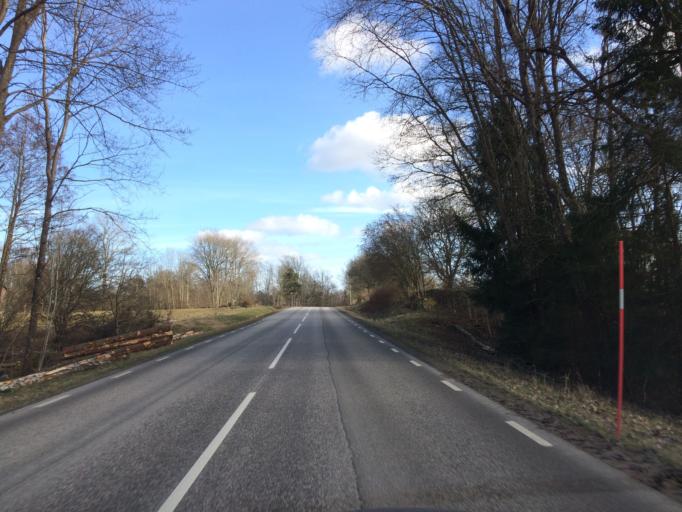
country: SE
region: Kronoberg
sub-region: Almhults Kommun
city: AElmhult
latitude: 56.5748
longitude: 14.1110
